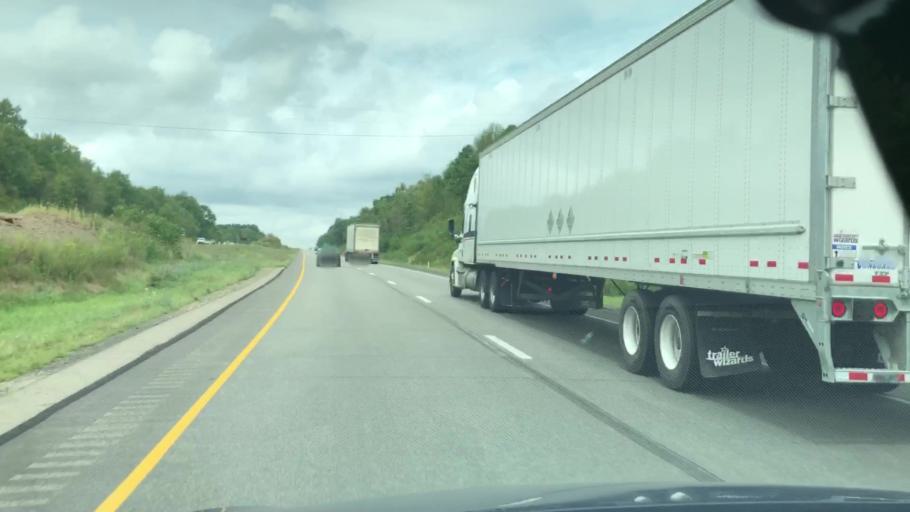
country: US
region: Pennsylvania
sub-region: Crawford County
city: Meadville
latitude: 41.5535
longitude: -80.1807
